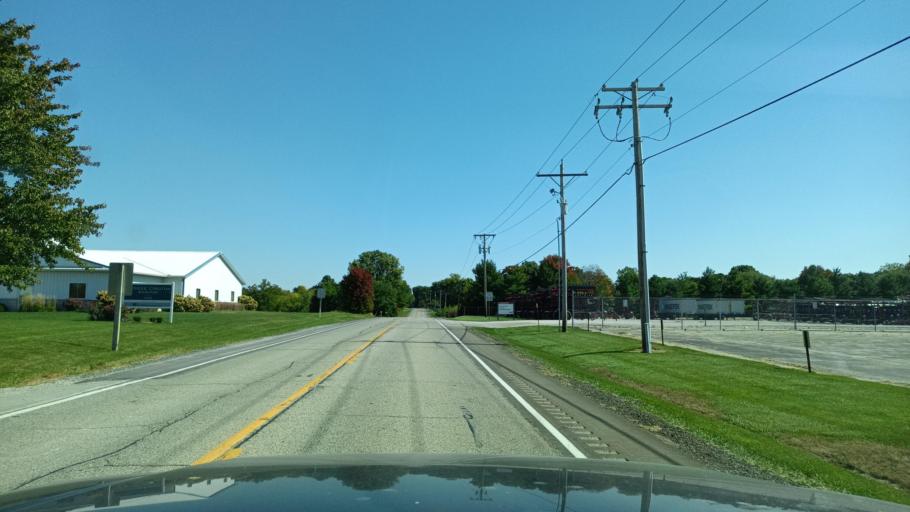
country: US
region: Illinois
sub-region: Woodford County
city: Eureka
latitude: 40.6273
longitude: -89.2614
